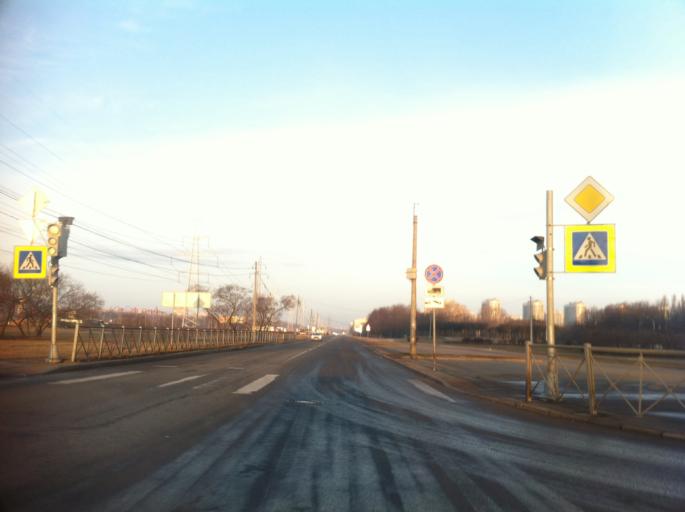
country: RU
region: St.-Petersburg
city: Uritsk
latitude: 59.8473
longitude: 30.1752
